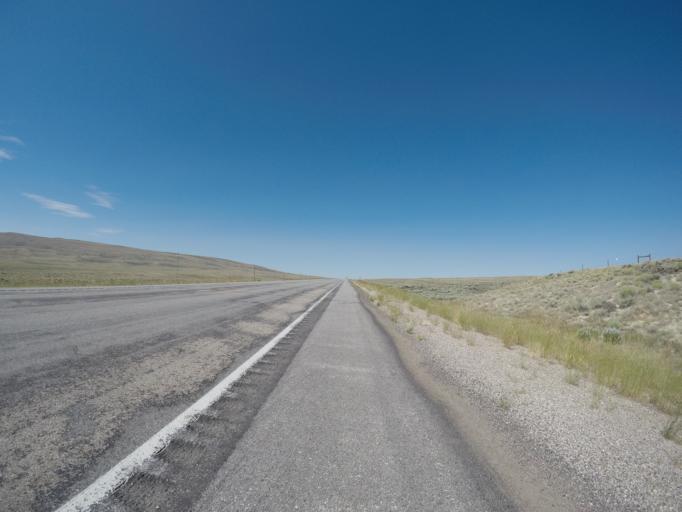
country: US
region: Wyoming
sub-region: Carbon County
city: Saratoga
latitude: 41.7997
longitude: -106.7127
